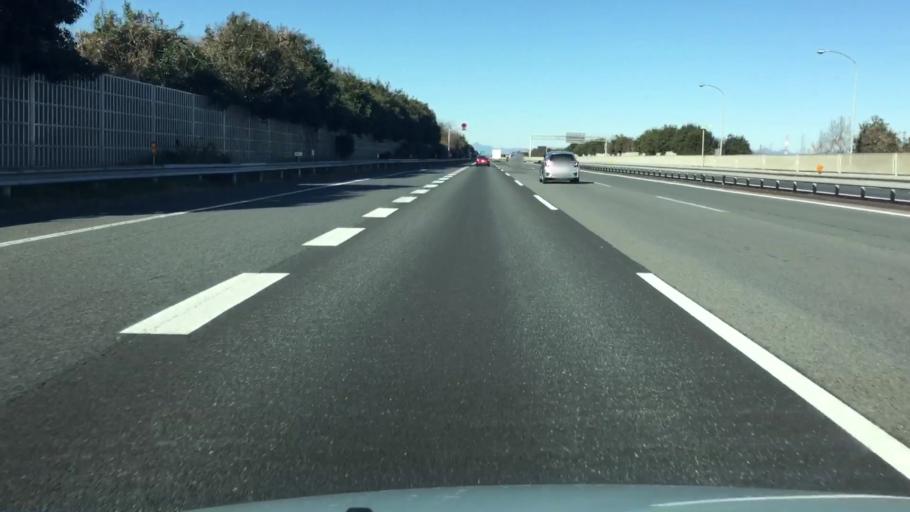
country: JP
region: Saitama
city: Yorii
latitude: 36.1254
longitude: 139.2465
